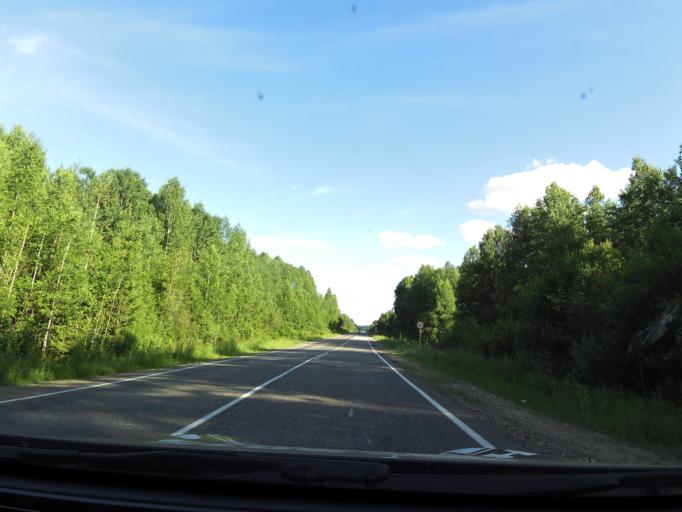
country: RU
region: Kirov
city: Omutninsk
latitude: 58.7481
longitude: 52.0607
